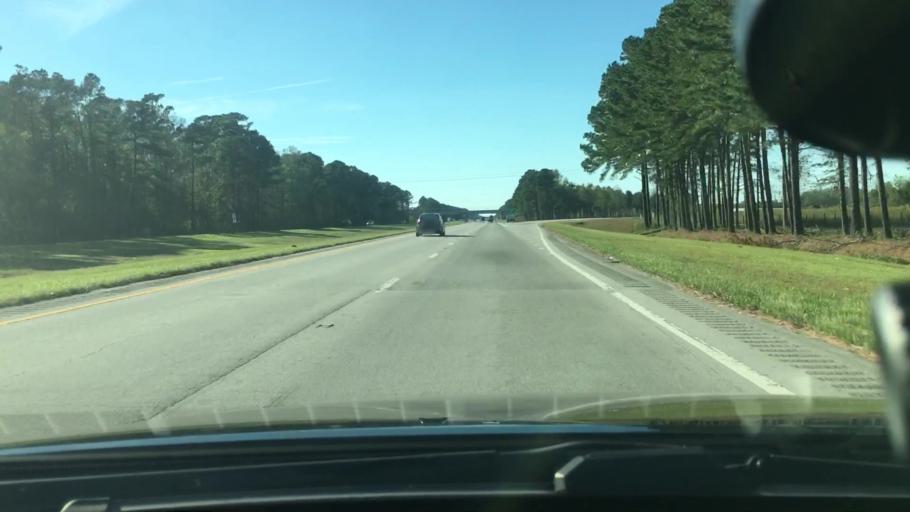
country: US
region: North Carolina
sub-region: Craven County
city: Trent Woods
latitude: 35.1248
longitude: -77.1260
